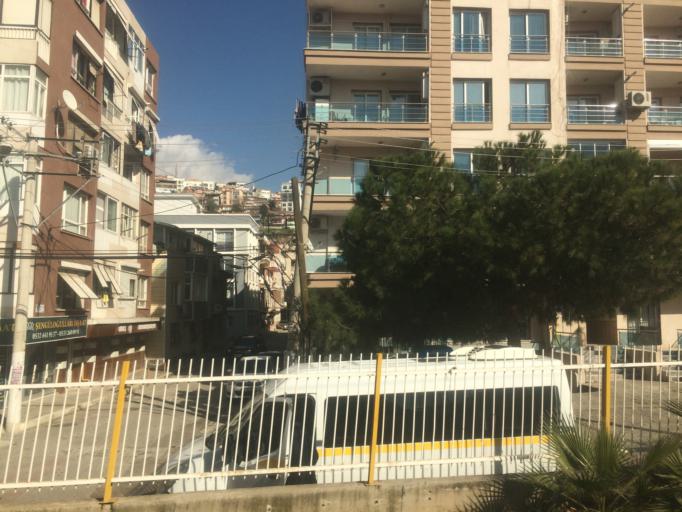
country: TR
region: Izmir
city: Karsiyaka
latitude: 38.4673
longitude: 27.1612
